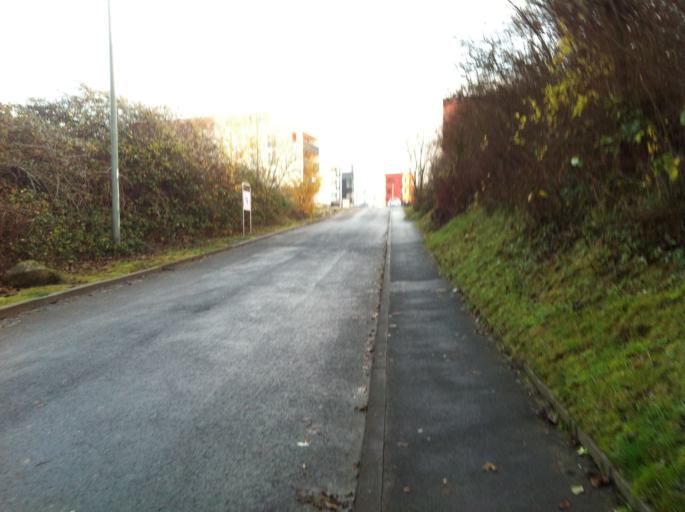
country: DE
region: Hesse
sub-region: Regierungsbezirk Darmstadt
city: Steinbach am Taunus
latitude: 50.1721
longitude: 8.6261
